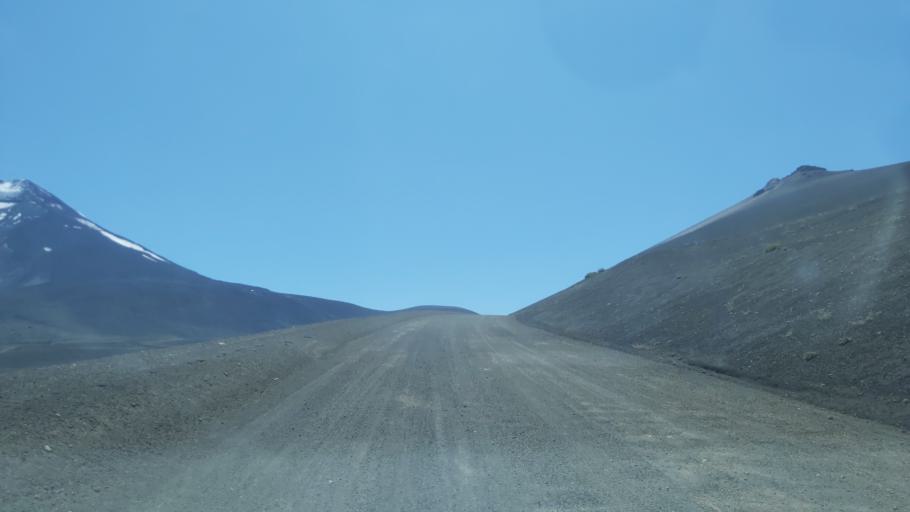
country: CL
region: Araucania
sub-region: Provincia de Cautin
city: Vilcun
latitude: -38.4116
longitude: -71.5420
